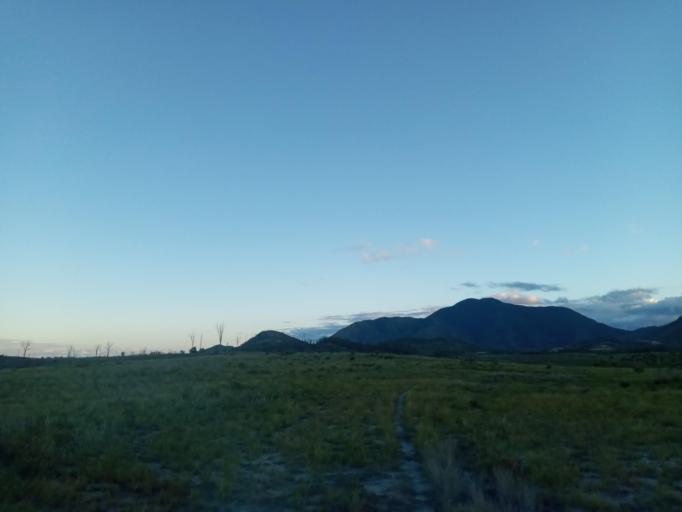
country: MG
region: Anosy
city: Fort Dauphin
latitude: -24.5138
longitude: 47.2344
